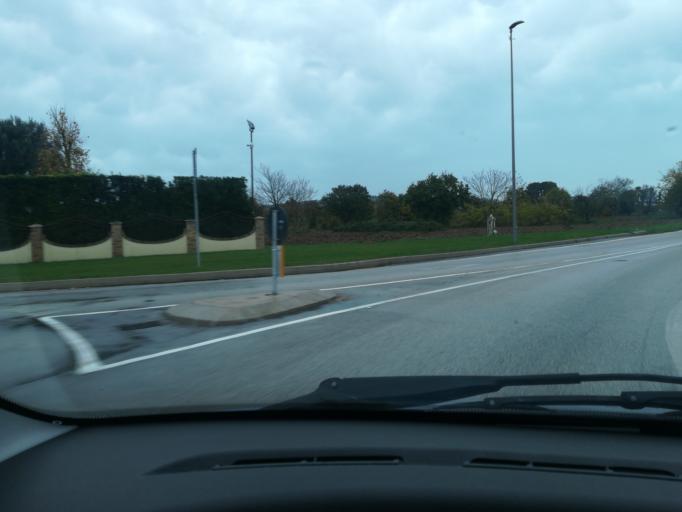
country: IT
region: The Marches
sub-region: Provincia di Macerata
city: Borgo Stazione
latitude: 43.2903
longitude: 13.6548
